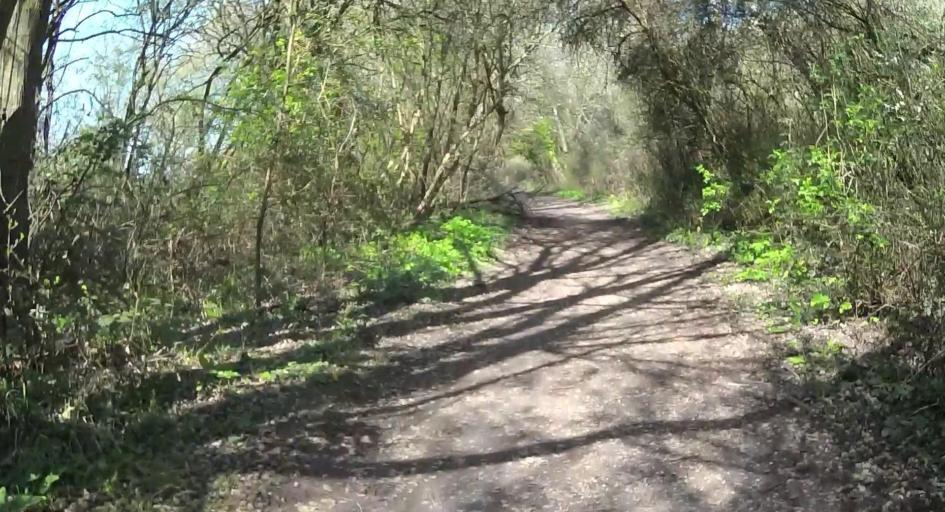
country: GB
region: England
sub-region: Hampshire
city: Romsey
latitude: 51.0799
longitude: -1.5024
